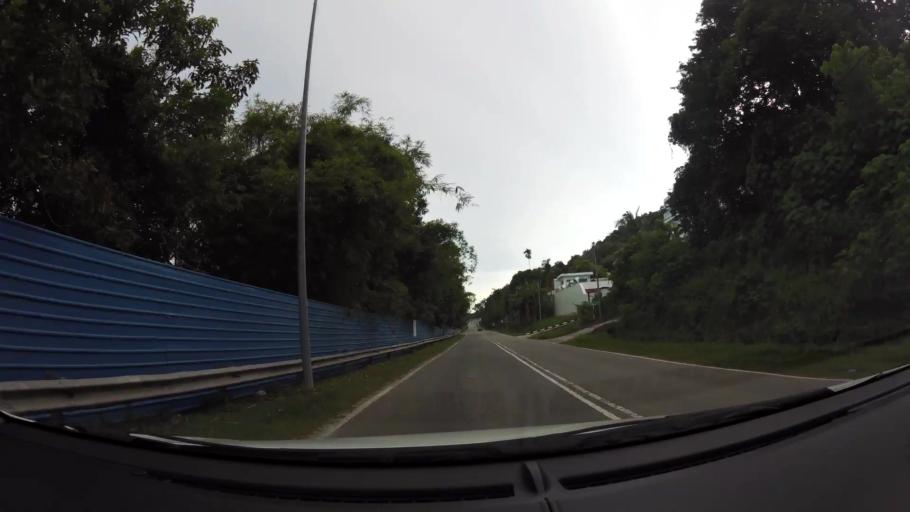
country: BN
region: Brunei and Muara
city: Bandar Seri Begawan
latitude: 4.9294
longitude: 115.0153
